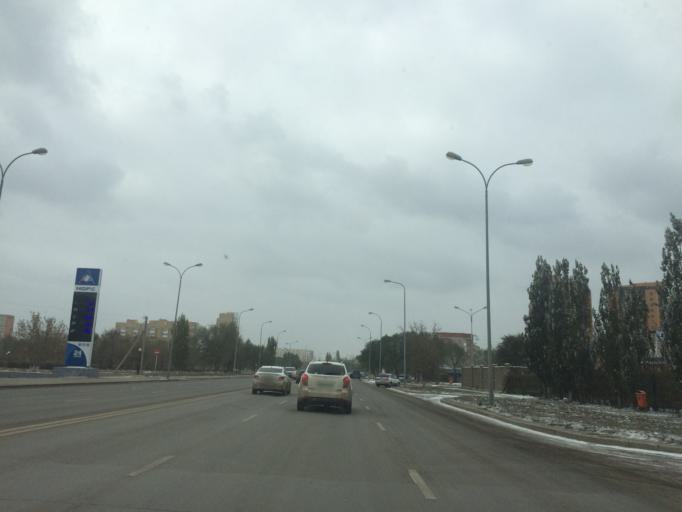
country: KZ
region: Astana Qalasy
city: Astana
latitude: 51.1675
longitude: 71.4771
